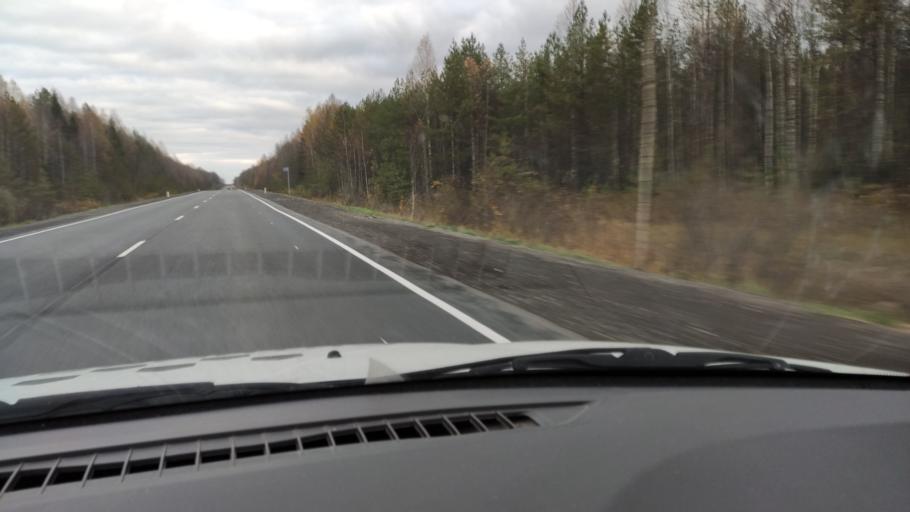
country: RU
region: Kirov
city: Chernaya Kholunitsa
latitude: 58.8812
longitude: 51.4333
